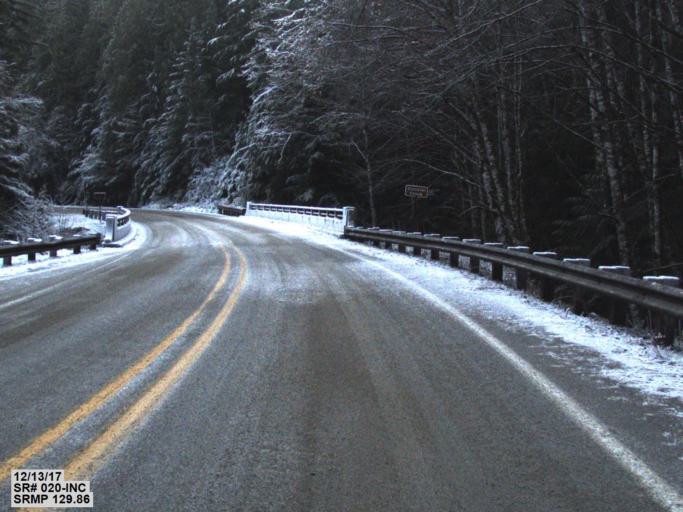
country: US
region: Washington
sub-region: Snohomish County
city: Darrington
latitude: 48.6909
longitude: -121.1045
